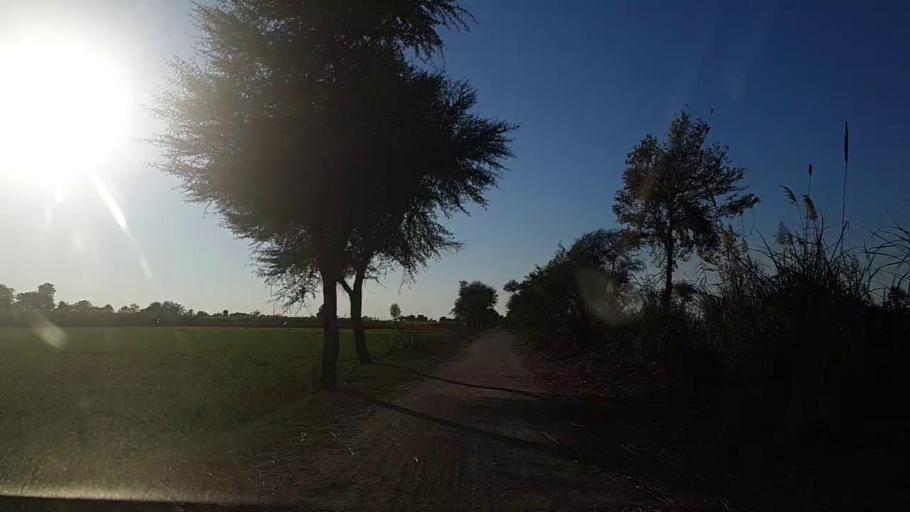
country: PK
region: Sindh
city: Sanghar
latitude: 26.1393
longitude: 68.9458
